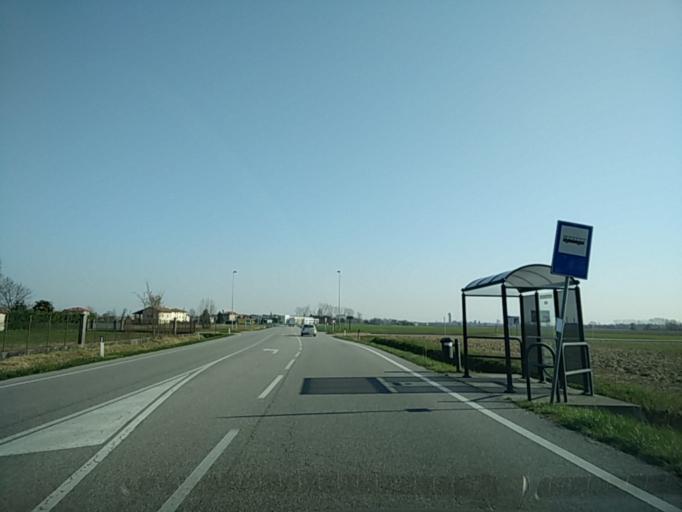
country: IT
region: Friuli Venezia Giulia
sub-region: Provincia di Pordenone
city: Villotta
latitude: 45.8753
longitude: 12.7764
